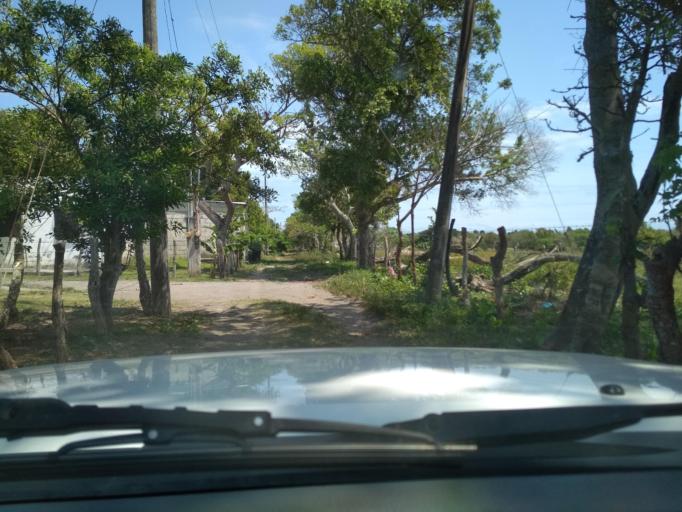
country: MX
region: Veracruz
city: Anton Lizardo
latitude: 19.0013
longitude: -95.9914
